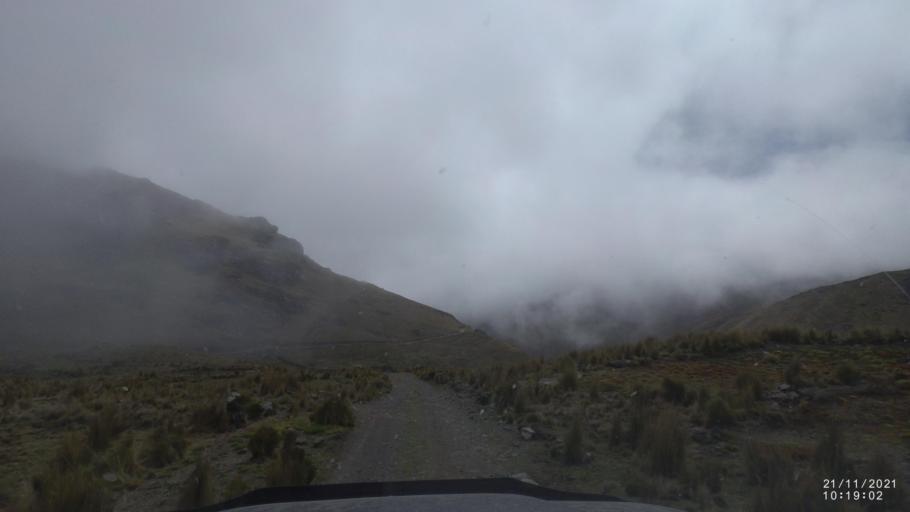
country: BO
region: Cochabamba
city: Cochabamba
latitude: -16.9918
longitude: -66.2652
